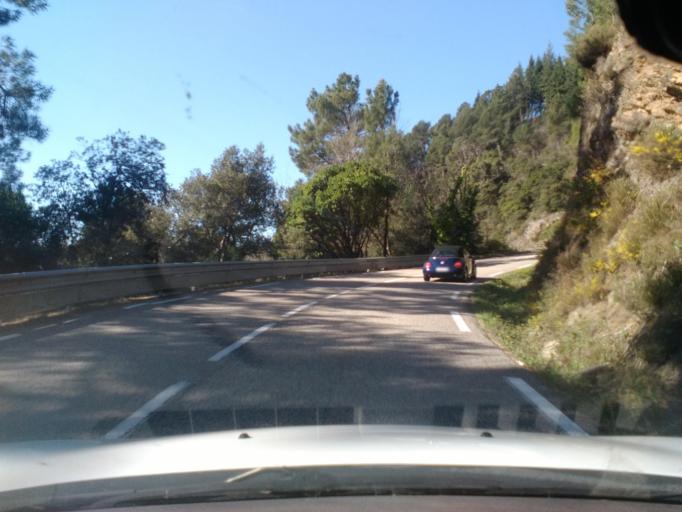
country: FR
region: Languedoc-Roussillon
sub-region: Departement du Gard
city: Saint-Jean-du-Gard
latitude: 44.1240
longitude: 3.8605
